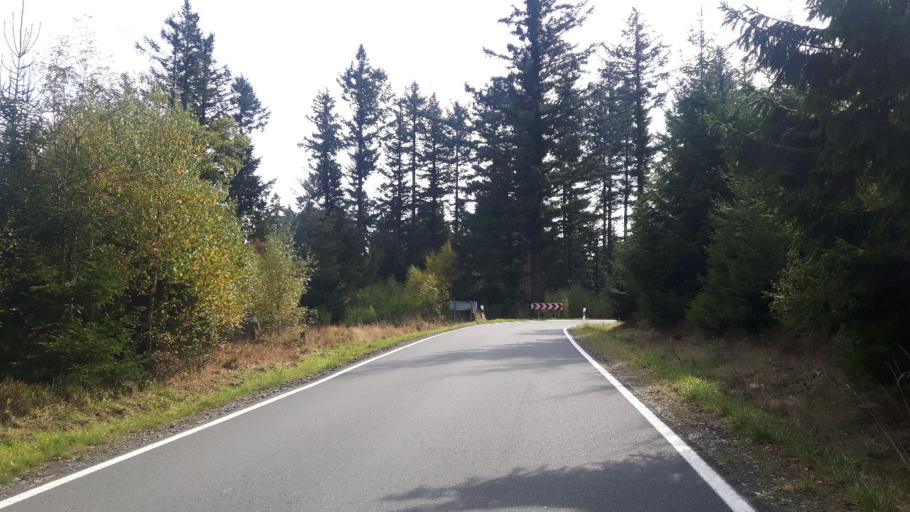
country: DE
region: North Rhine-Westphalia
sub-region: Regierungsbezirk Arnsberg
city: Erndtebruck
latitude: 50.9050
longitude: 8.2452
